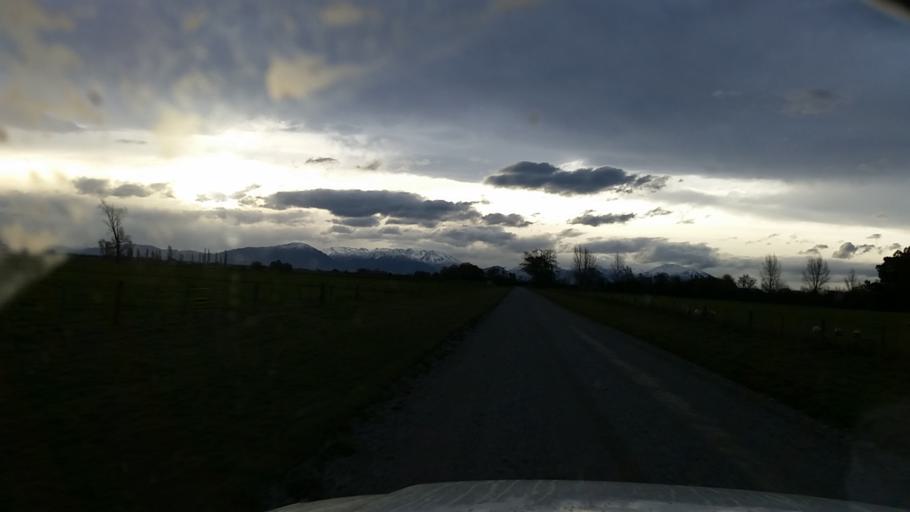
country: NZ
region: Canterbury
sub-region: Ashburton District
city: Ashburton
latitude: -43.8405
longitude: 171.6571
